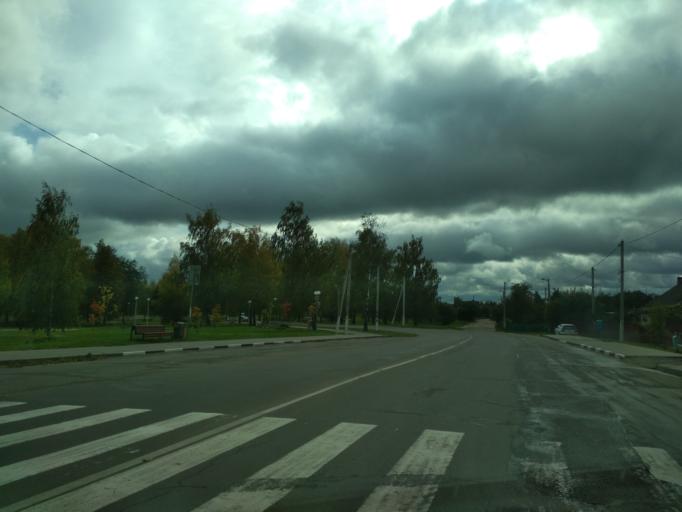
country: BY
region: Minsk
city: Mar''ina Horka
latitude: 53.5070
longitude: 28.1541
